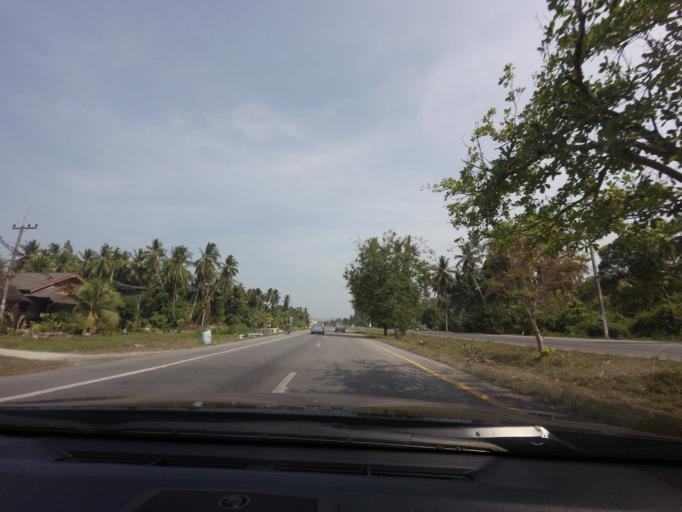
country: TH
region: Pattani
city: Yaring
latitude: 6.8357
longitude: 101.3855
